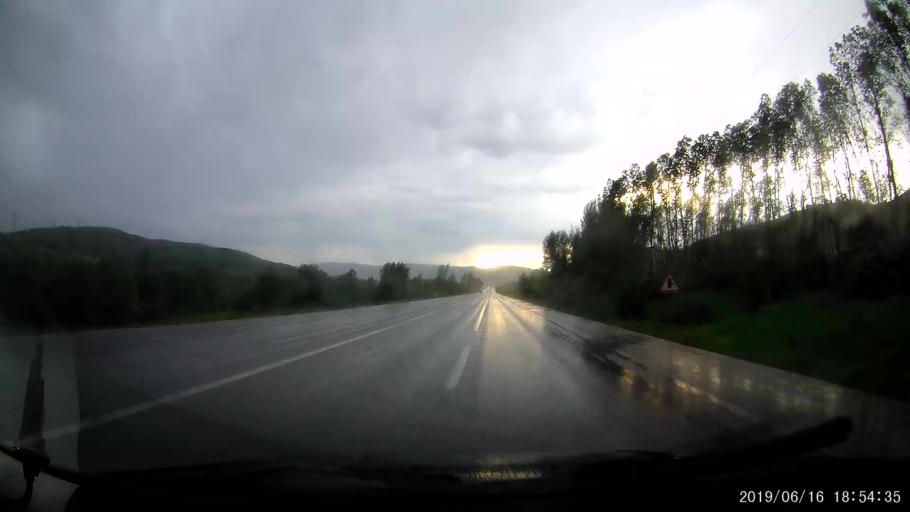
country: TR
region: Erzincan
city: Catalcam
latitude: 39.8973
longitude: 38.8501
